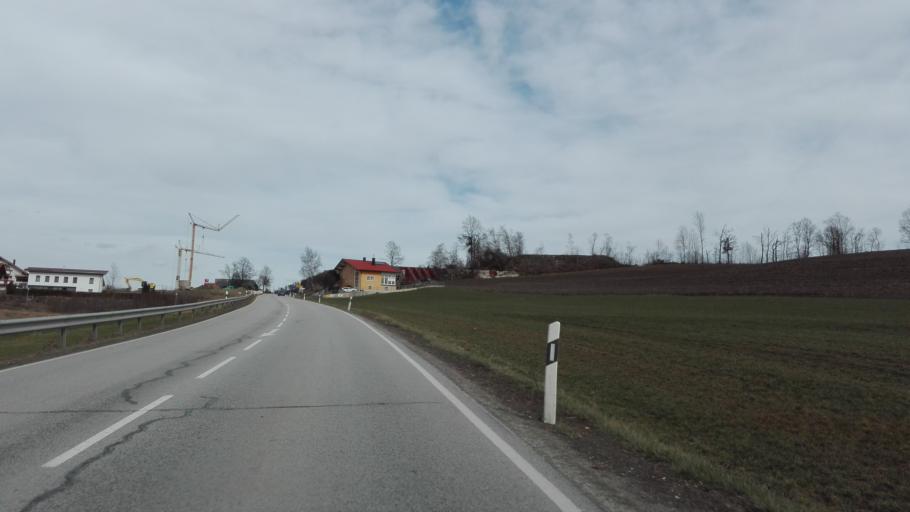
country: DE
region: Bavaria
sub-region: Lower Bavaria
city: Hauzenberg
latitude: 48.6471
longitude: 13.6164
